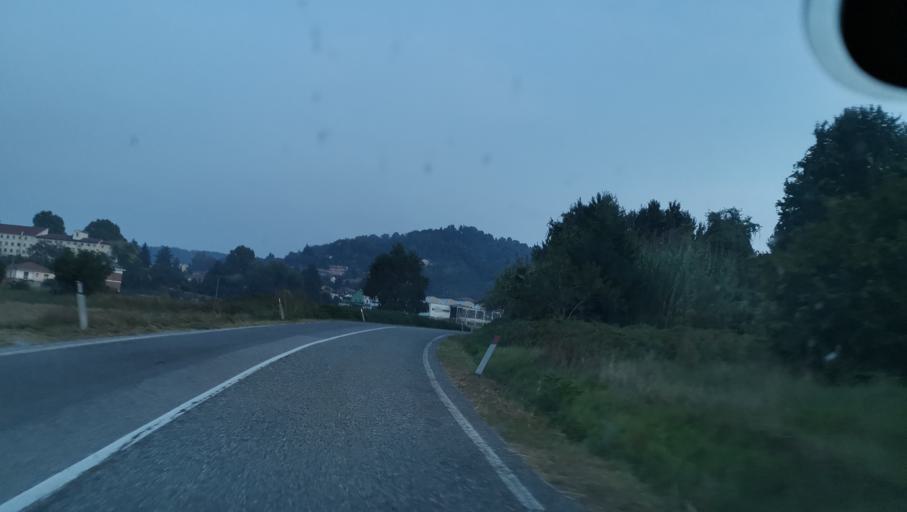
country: IT
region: Piedmont
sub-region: Provincia di Torino
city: Castiglione Torinese
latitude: 45.1270
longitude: 7.8144
